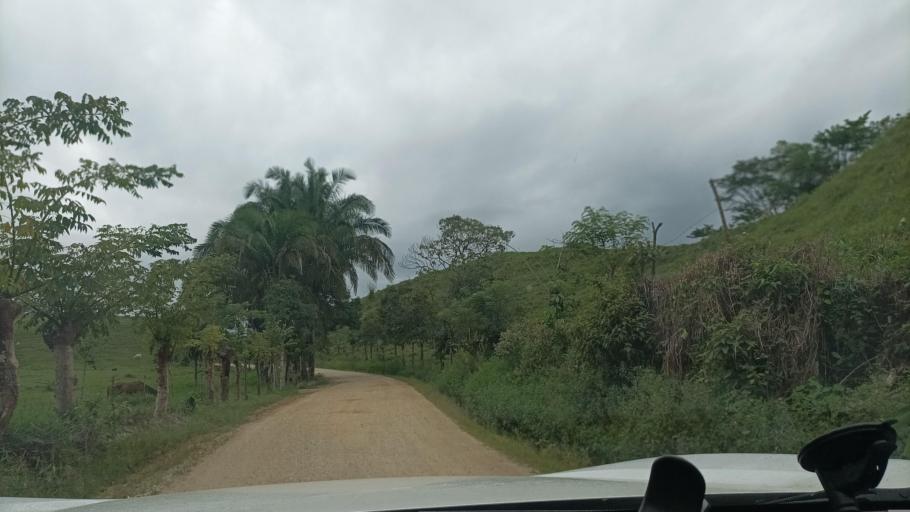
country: MX
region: Veracruz
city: Hidalgotitlan
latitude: 17.6251
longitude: -94.5121
